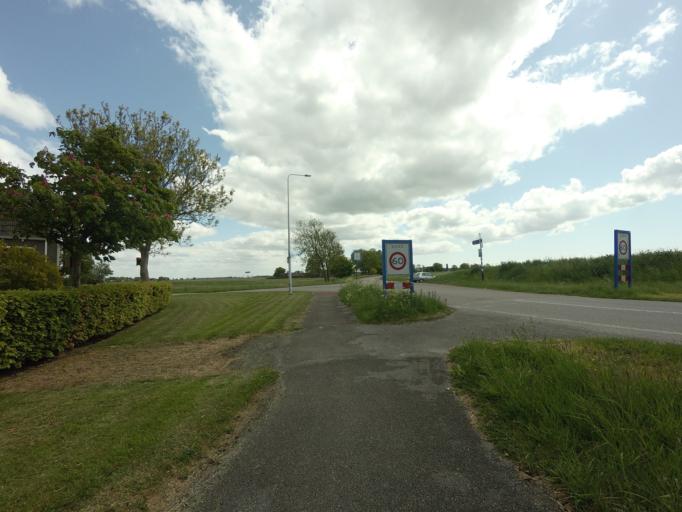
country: NL
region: Friesland
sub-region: Sudwest Fryslan
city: Bolsward
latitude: 53.0927
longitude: 5.5349
